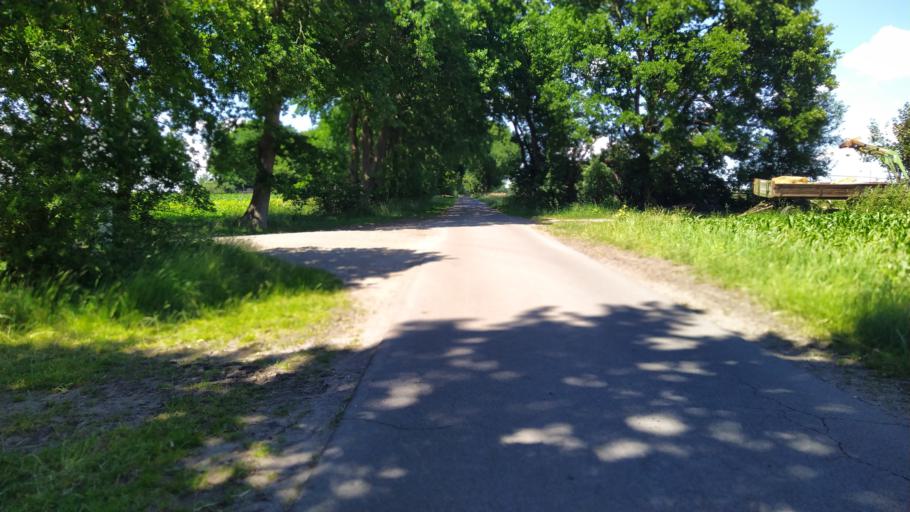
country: DE
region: Lower Saxony
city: Estorf
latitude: 53.5659
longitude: 9.2078
